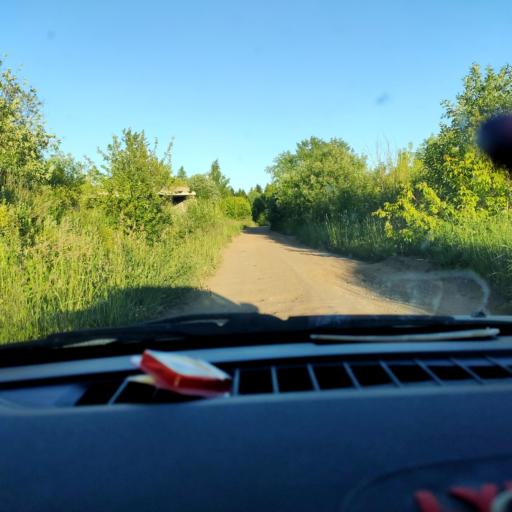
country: RU
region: Perm
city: Froly
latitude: 57.9449
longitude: 56.1980
